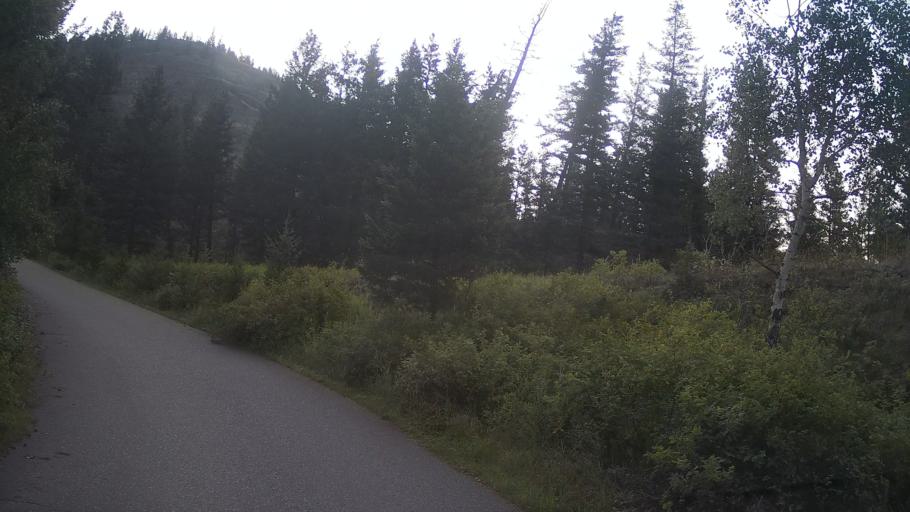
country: CA
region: British Columbia
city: Hanceville
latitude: 52.0875
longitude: -123.3956
